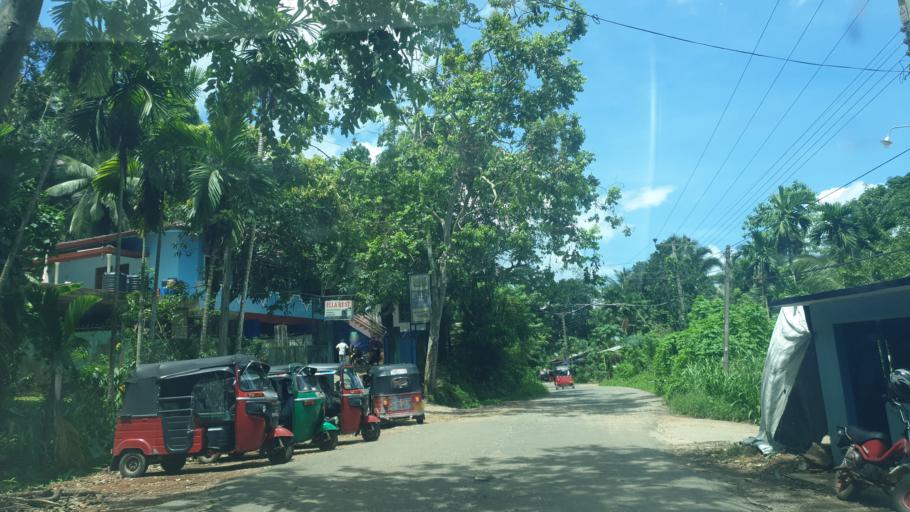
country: LK
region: Sabaragamuwa
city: Ratnapura
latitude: 6.4847
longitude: 80.4061
